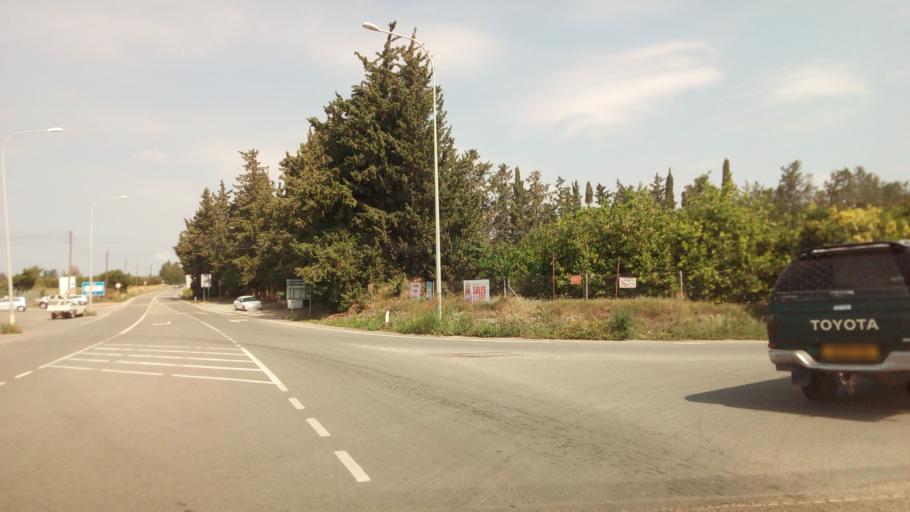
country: CY
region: Pafos
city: Paphos
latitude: 34.7229
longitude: 32.5276
